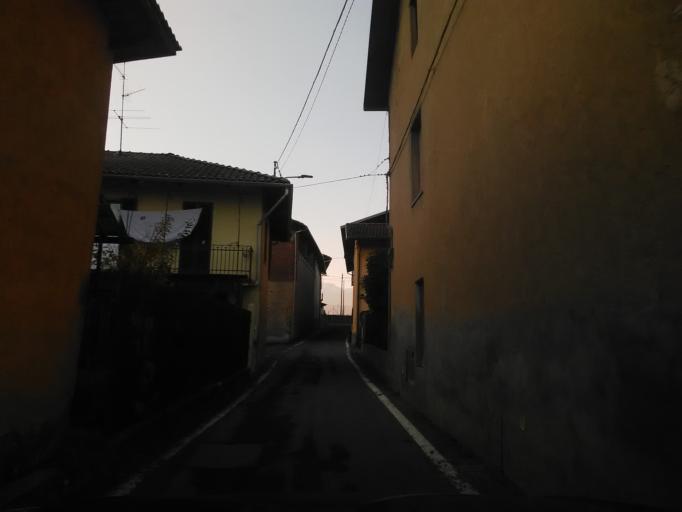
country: IT
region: Piedmont
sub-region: Provincia di Biella
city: Cerrione
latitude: 45.4704
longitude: 8.0669
